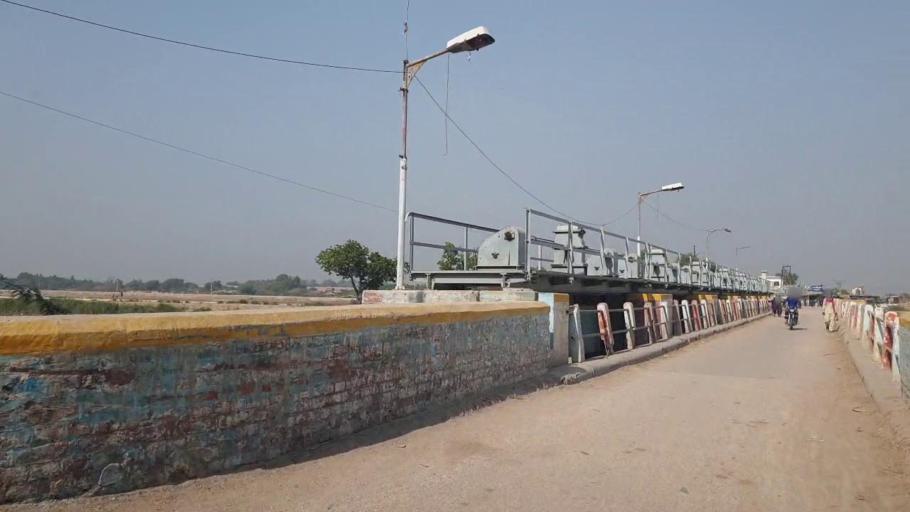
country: PK
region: Sindh
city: Jamshoro
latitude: 25.4401
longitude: 68.3330
